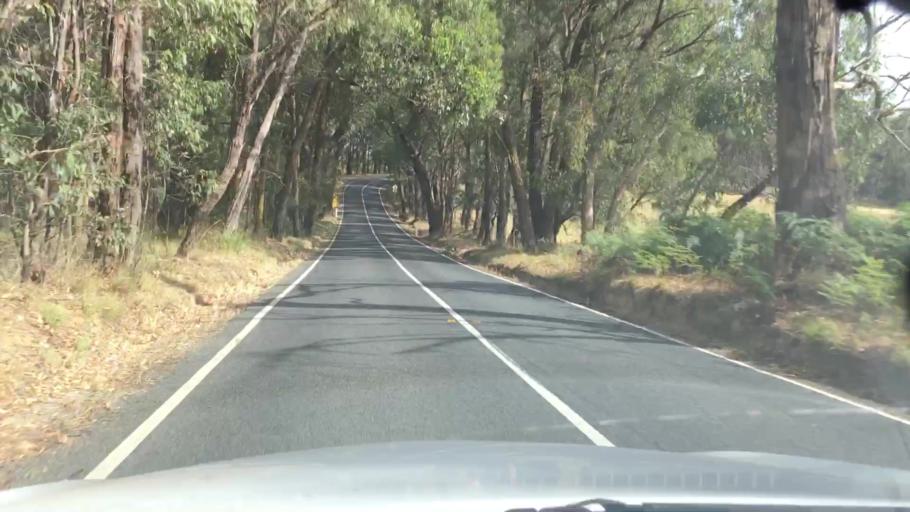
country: AU
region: Victoria
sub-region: Yarra Ranges
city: Macclesfield
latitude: -37.8475
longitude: 145.4858
